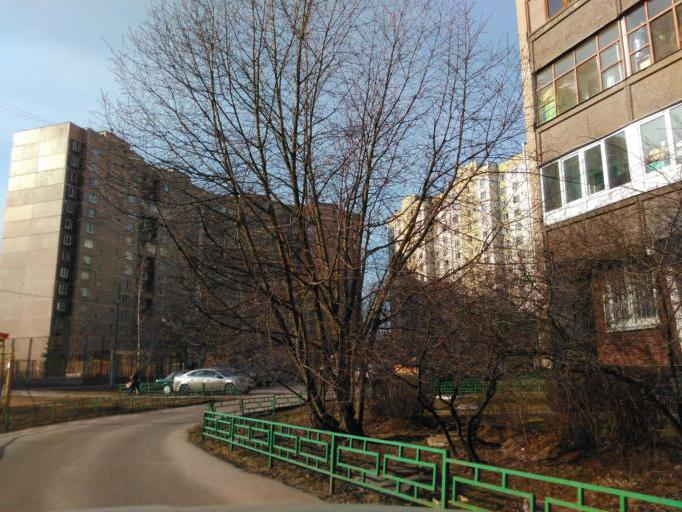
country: RU
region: Moskovskaya
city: Andreyevka
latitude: 55.9719
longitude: 37.1513
